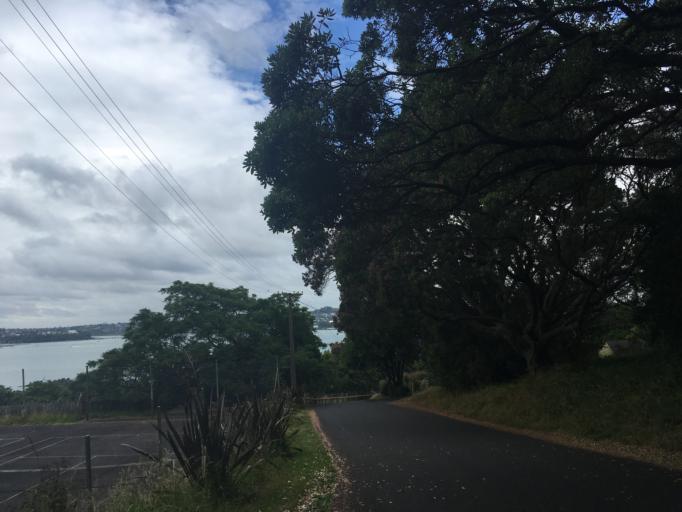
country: NZ
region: Auckland
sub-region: Auckland
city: Auckland
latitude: -36.8272
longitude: 174.7992
